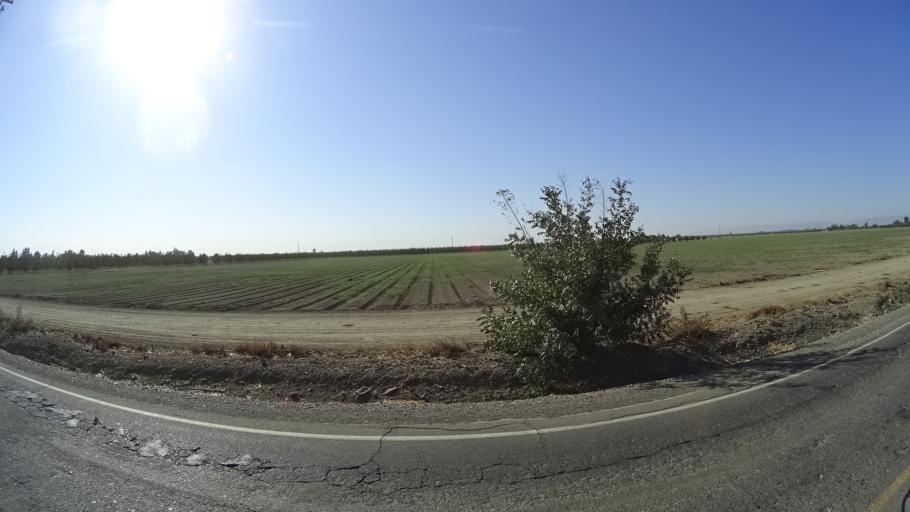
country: US
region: California
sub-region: Yolo County
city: Woodland
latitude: 38.6630
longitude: -121.8087
